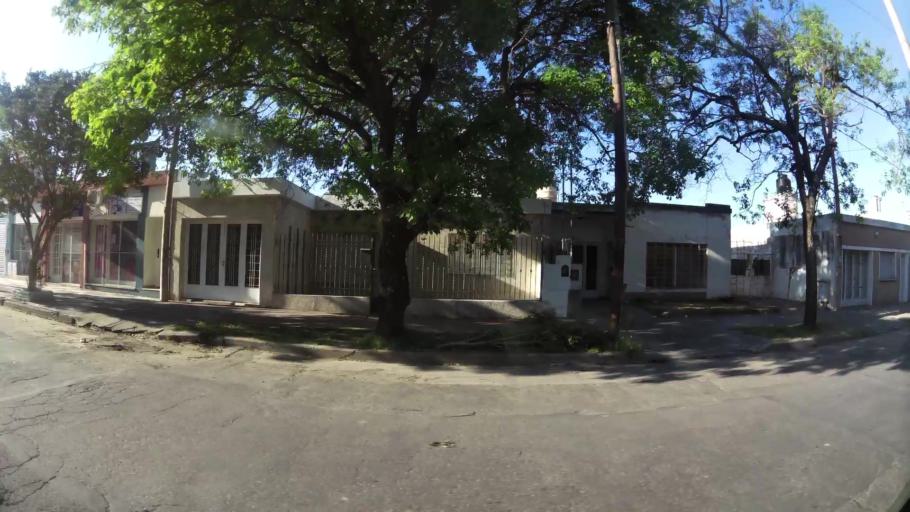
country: AR
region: Cordoba
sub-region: Departamento de Capital
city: Cordoba
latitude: -31.3805
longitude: -64.1791
